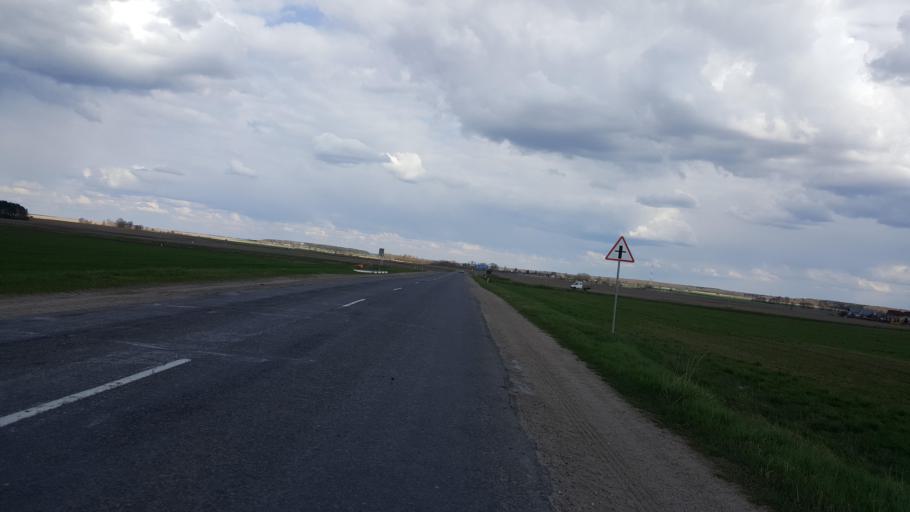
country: BY
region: Brest
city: Kamyanyets
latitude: 52.4149
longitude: 23.6340
